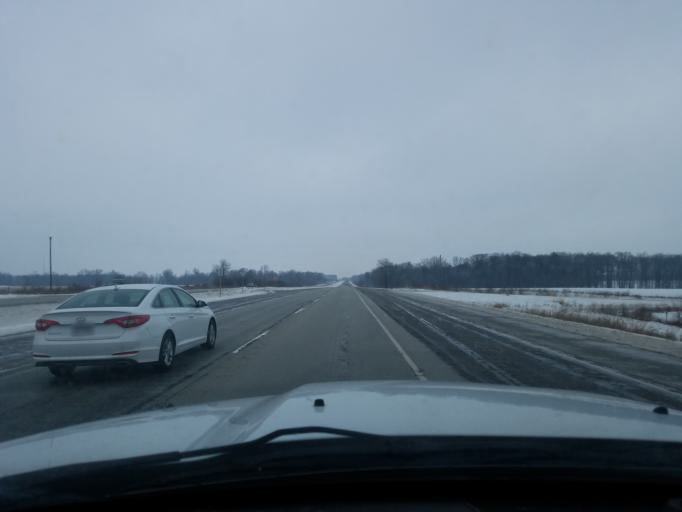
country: US
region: Indiana
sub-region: Fulton County
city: Rochester
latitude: 41.1418
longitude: -86.2397
